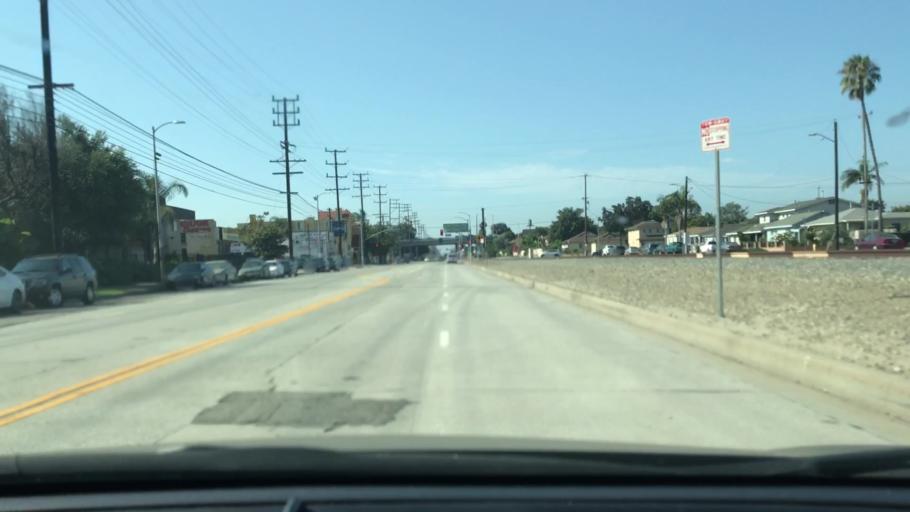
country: US
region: California
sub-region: Los Angeles County
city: Gardena
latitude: 33.8636
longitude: -118.2993
